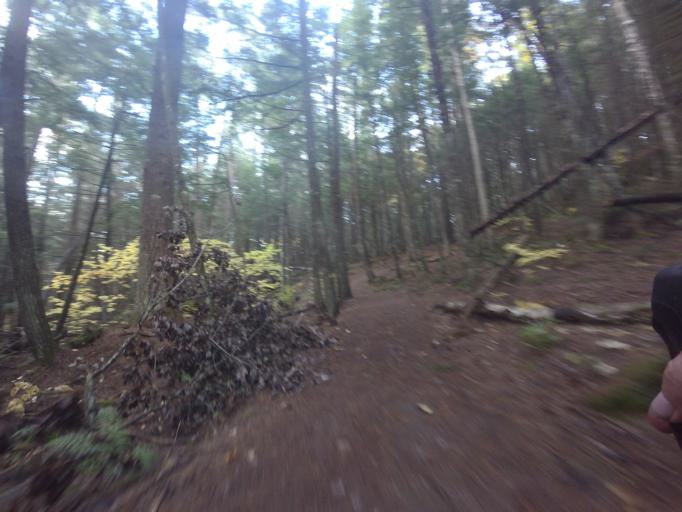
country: CA
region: Ontario
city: Deep River
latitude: 45.8882
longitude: -77.6346
